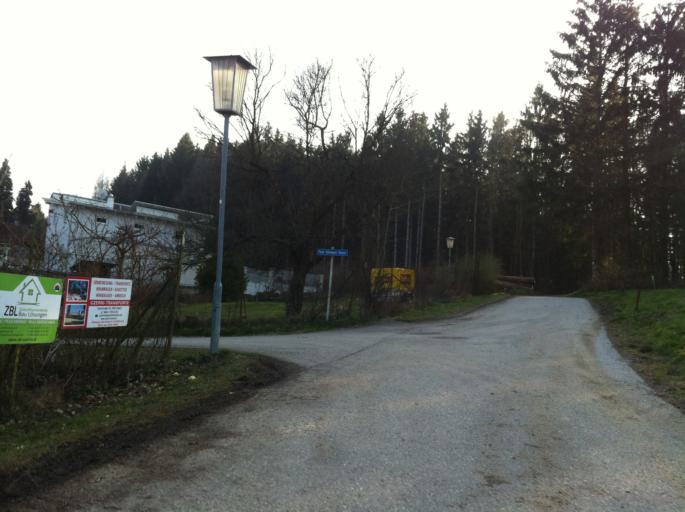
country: AT
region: Lower Austria
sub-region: Politischer Bezirk Wien-Umgebung
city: Pressbaum
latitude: 48.1801
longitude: 16.1047
